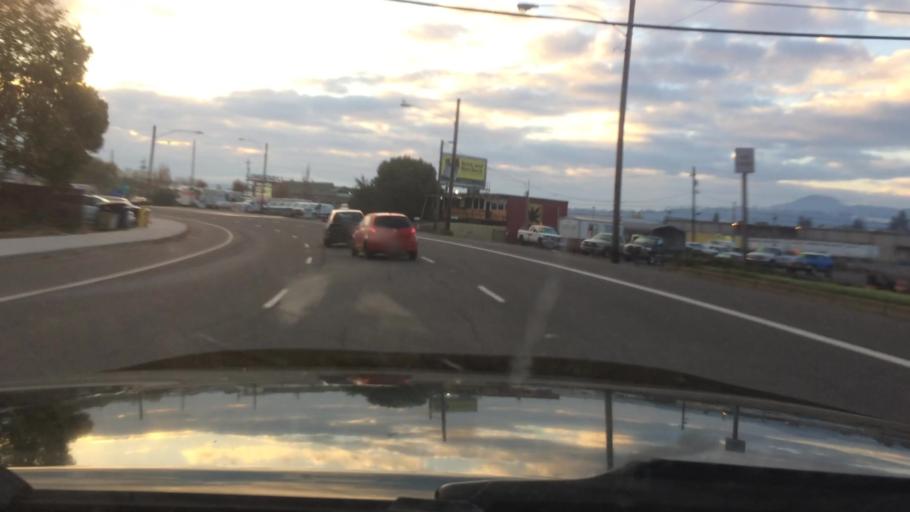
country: US
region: Oregon
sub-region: Lane County
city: Eugene
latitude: 44.0529
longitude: -123.1269
